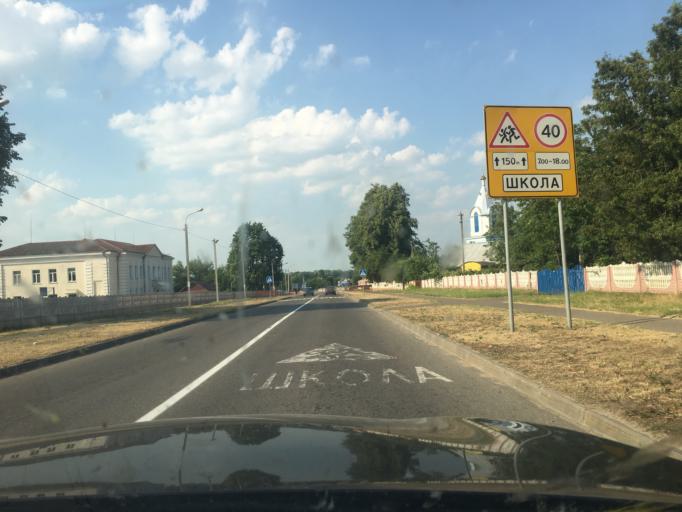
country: BY
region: Grodnenskaya
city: Indura
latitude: 53.3390
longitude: 23.9477
